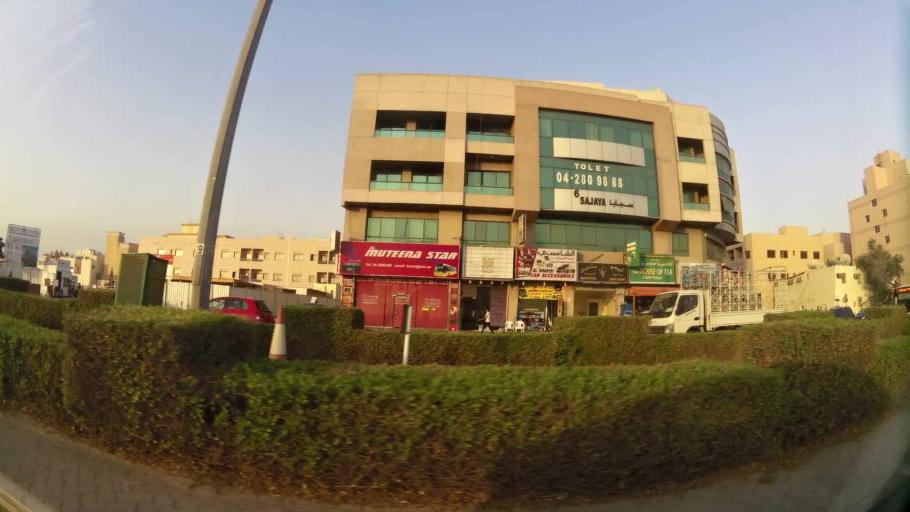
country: AE
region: Ash Shariqah
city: Sharjah
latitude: 25.2754
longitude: 55.3291
